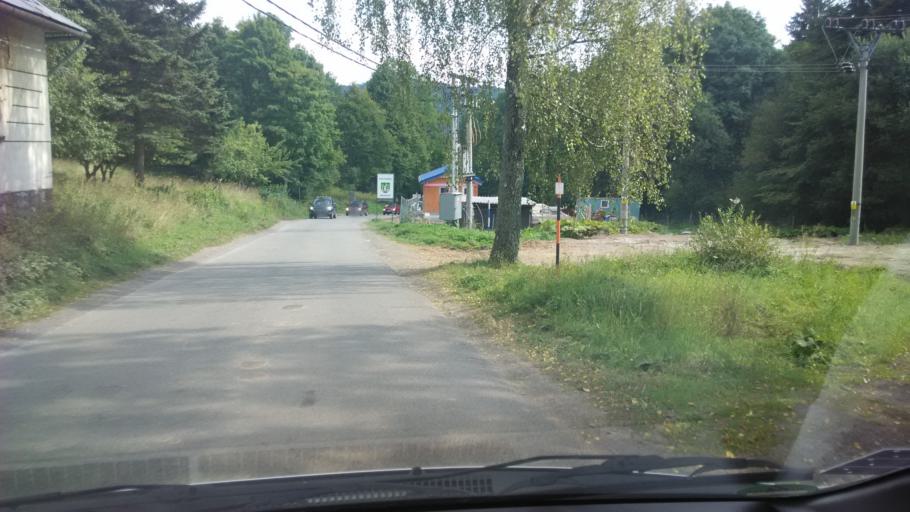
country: SK
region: Banskobystricky
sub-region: Okres Ziar nad Hronom
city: Kremnica
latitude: 48.7217
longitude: 18.9455
